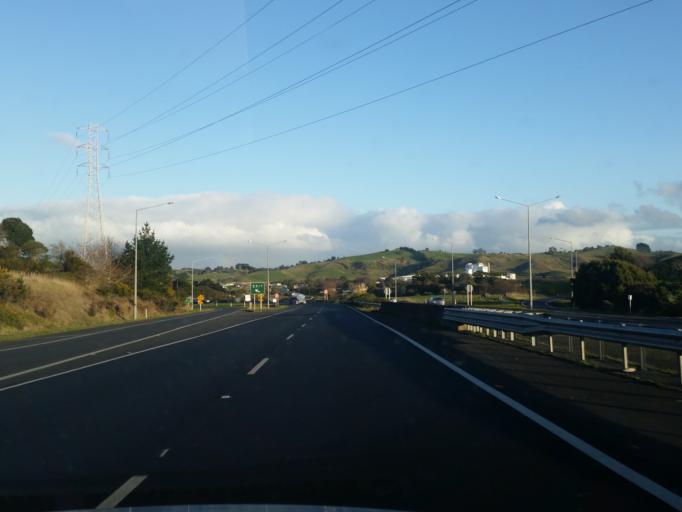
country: NZ
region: Auckland
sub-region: Auckland
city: Pukekohe East
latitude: -37.2365
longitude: 175.0205
